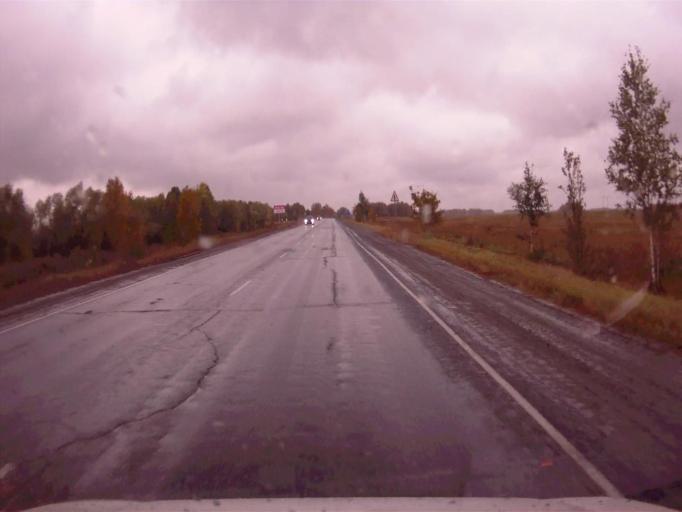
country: RU
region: Chelyabinsk
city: Roshchino
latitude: 55.3935
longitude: 61.1103
